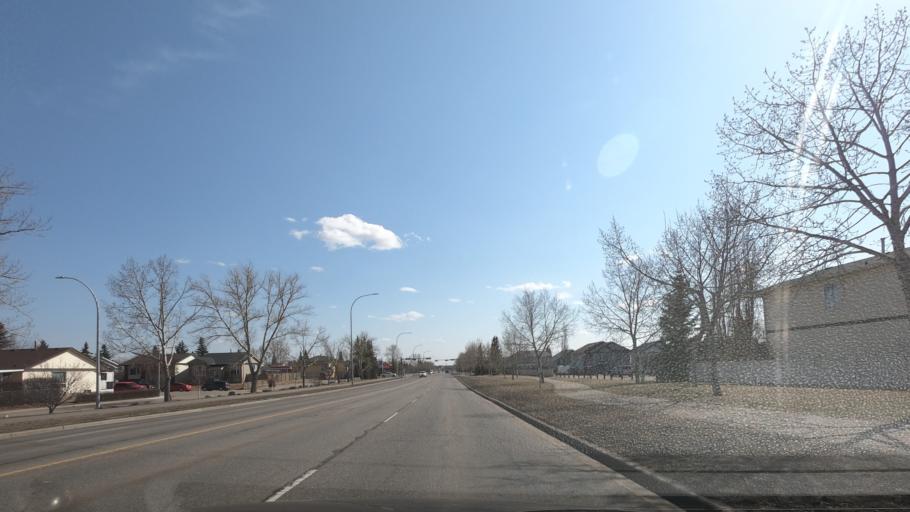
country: CA
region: Alberta
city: Airdrie
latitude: 51.2774
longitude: -113.9899
